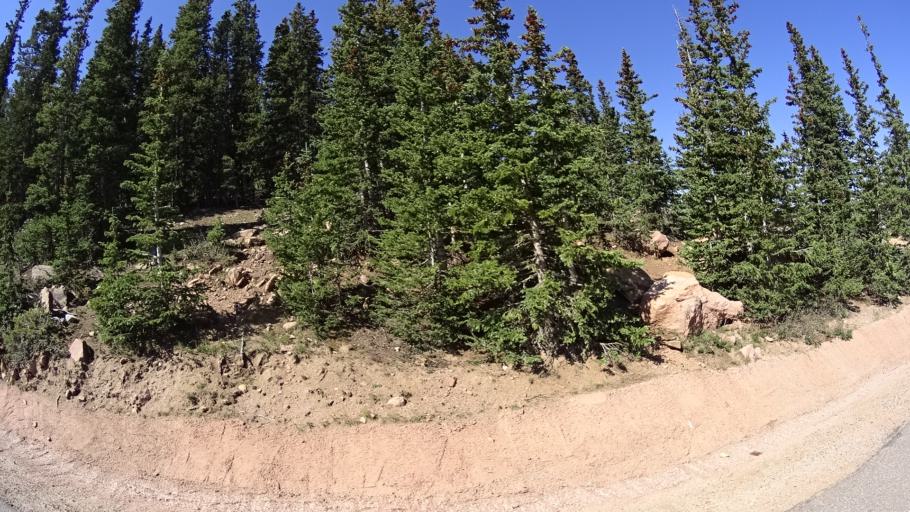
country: US
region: Colorado
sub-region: El Paso County
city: Cascade-Chipita Park
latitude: 38.8796
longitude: -105.0745
